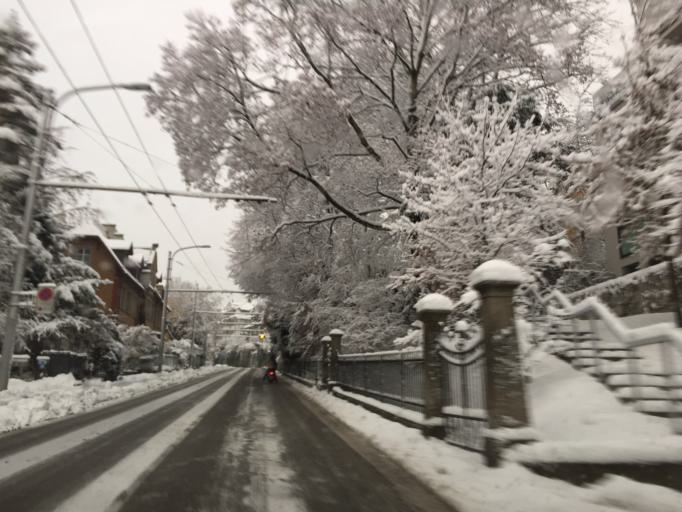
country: CH
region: Zurich
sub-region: Bezirk Zuerich
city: Zuerich (Kreis 7) / Hottingen
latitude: 47.3741
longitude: 8.5611
